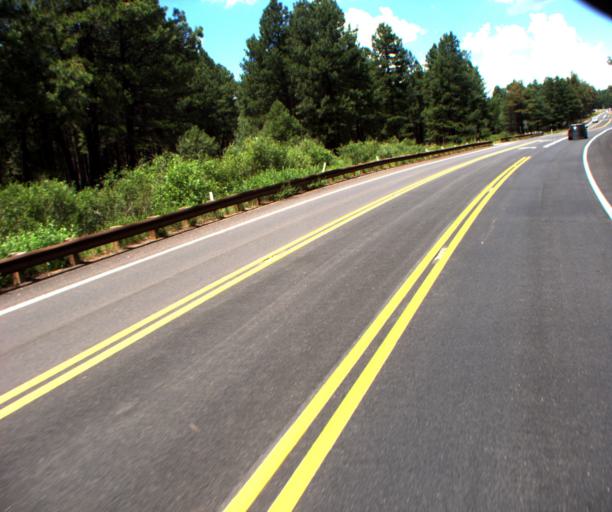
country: US
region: Arizona
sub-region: Coconino County
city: Flagstaff
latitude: 35.2411
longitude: -111.6838
